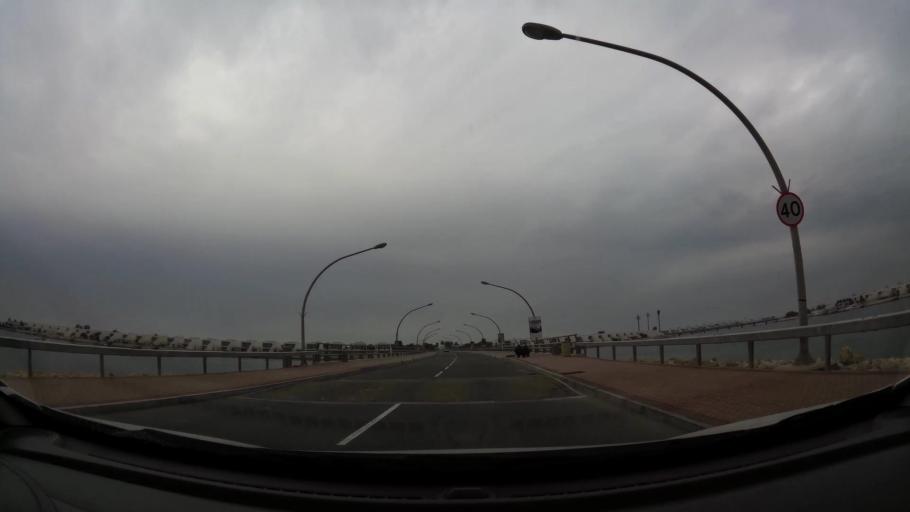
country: BH
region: Central Governorate
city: Dar Kulayb
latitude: 25.8408
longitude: 50.6148
